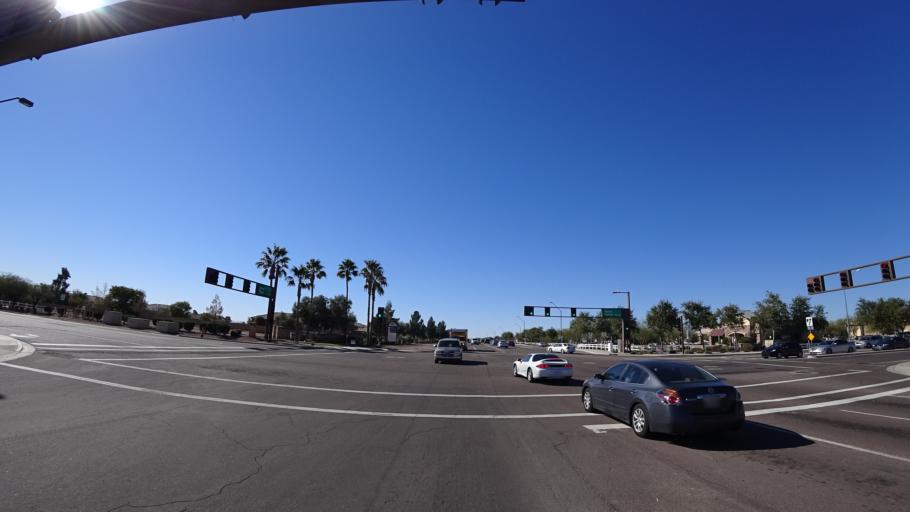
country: US
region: Arizona
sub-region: Maricopa County
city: Goodyear
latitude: 33.4355
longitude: -112.4093
